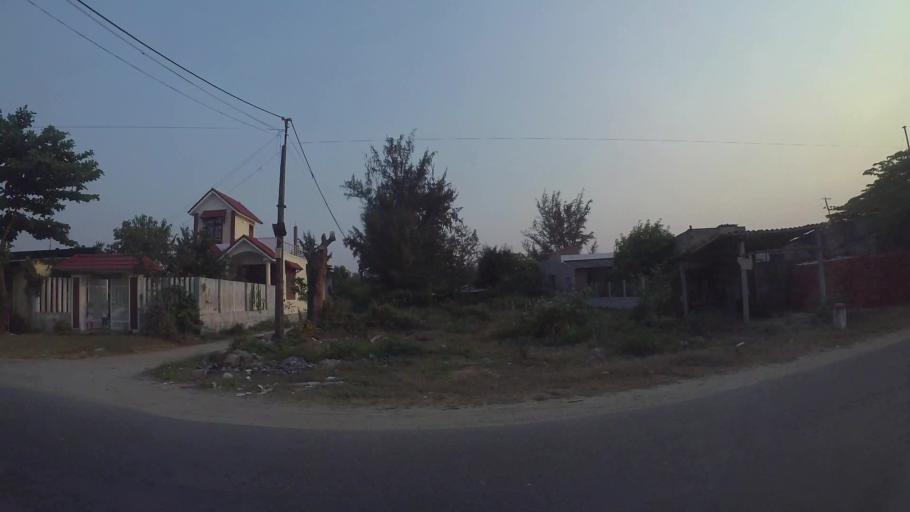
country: VN
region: Da Nang
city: Ngu Hanh Son
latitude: 15.9556
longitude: 108.2482
